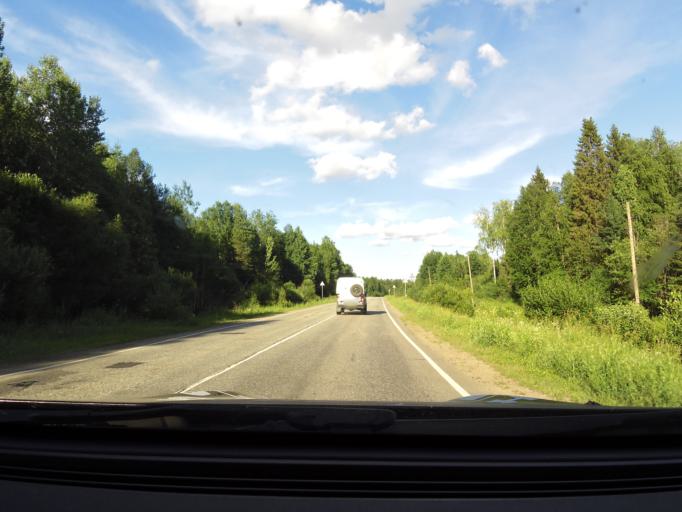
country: RU
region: Kirov
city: Belorechensk
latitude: 58.7157
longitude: 52.2885
